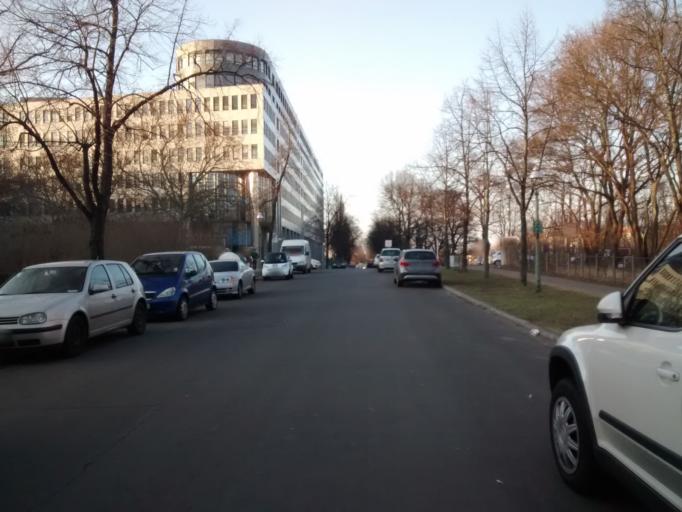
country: DE
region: Berlin
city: Charlottenburg-Nord
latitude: 52.5252
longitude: 13.3150
